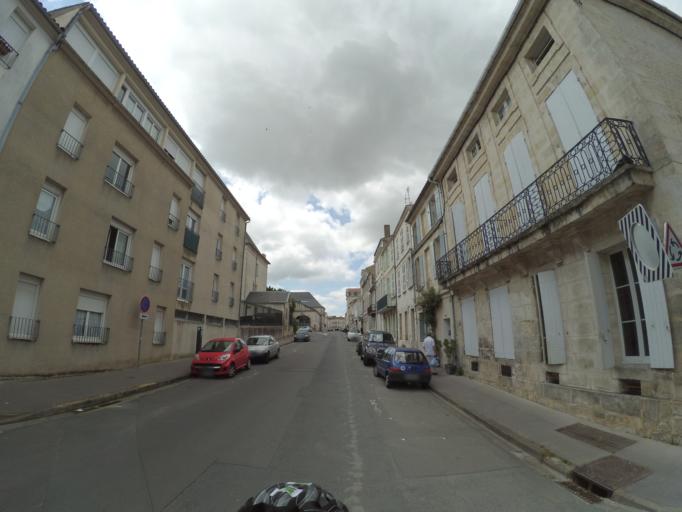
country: FR
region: Poitou-Charentes
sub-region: Departement de la Charente-Maritime
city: Rochefort
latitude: 45.9413
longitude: -0.9577
